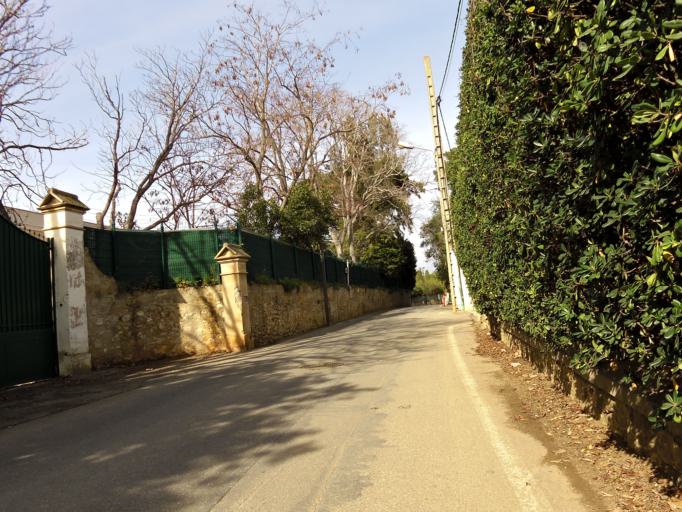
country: FR
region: Provence-Alpes-Cote d'Azur
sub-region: Departement des Alpes-Maritimes
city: Antibes
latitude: 43.5510
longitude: 7.1290
